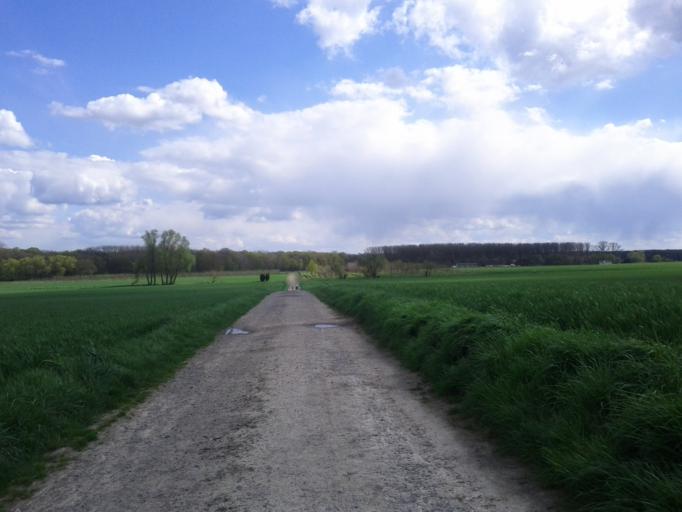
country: DE
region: North Rhine-Westphalia
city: Lanstrop
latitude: 51.5741
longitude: 7.5750
